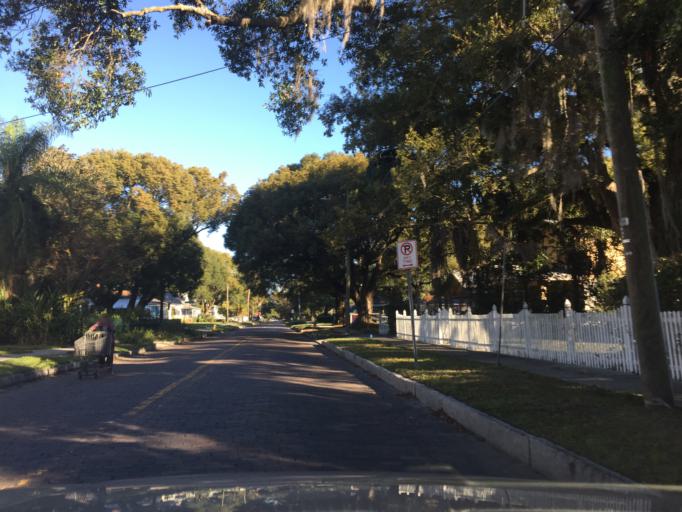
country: US
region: Florida
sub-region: Hillsborough County
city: Tampa
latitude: 27.9681
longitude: -82.4553
